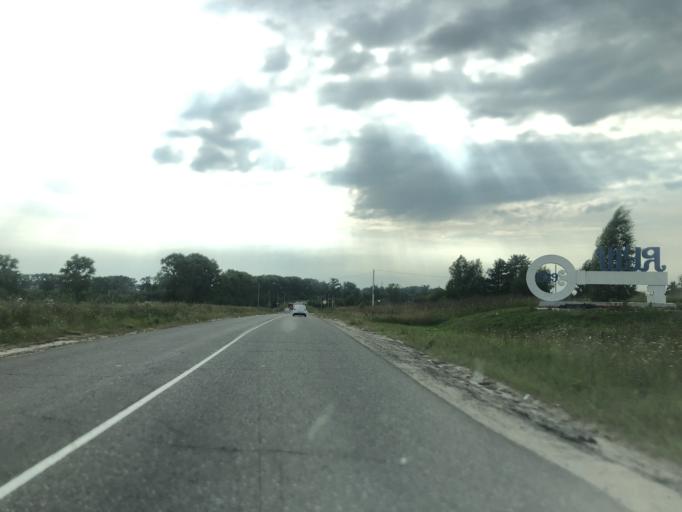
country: RU
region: Ivanovo
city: Shuya
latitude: 56.8573
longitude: 41.4372
